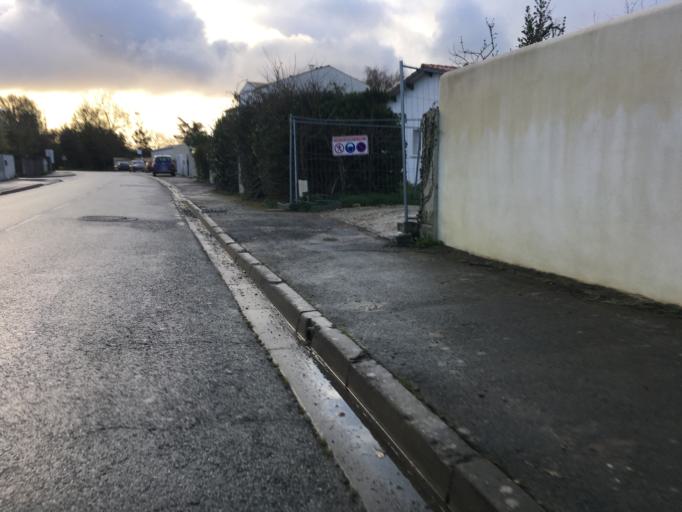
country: FR
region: Poitou-Charentes
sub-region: Departement de la Charente-Maritime
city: Nieul-sur-Mer
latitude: 46.1905
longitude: -1.1844
